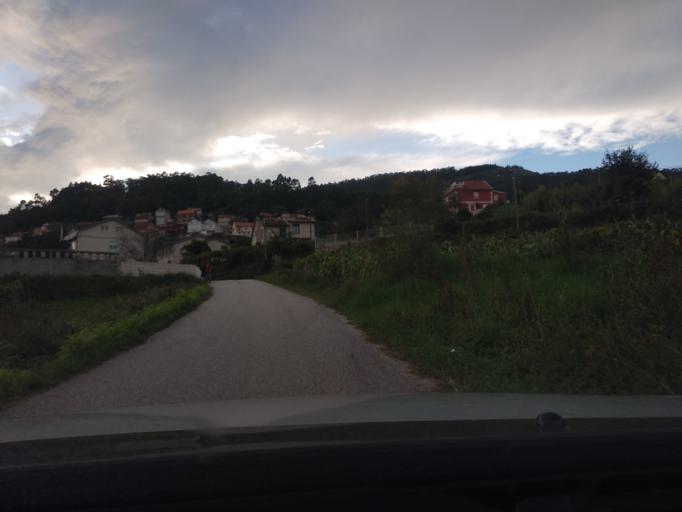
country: ES
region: Galicia
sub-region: Provincia de Pontevedra
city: Moana
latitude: 42.2984
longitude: -8.7363
